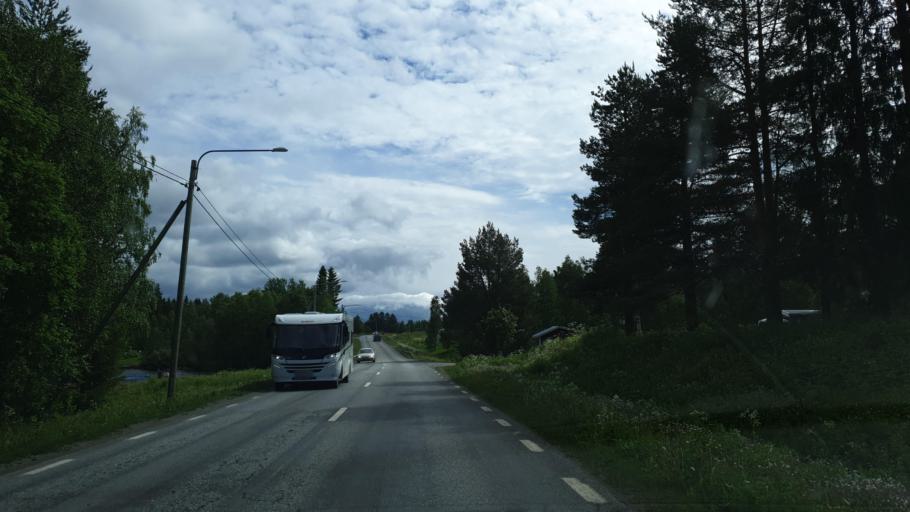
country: SE
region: Vaesterbotten
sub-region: Vilhelmina Kommun
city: Sjoberg
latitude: 64.6445
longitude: 16.3518
